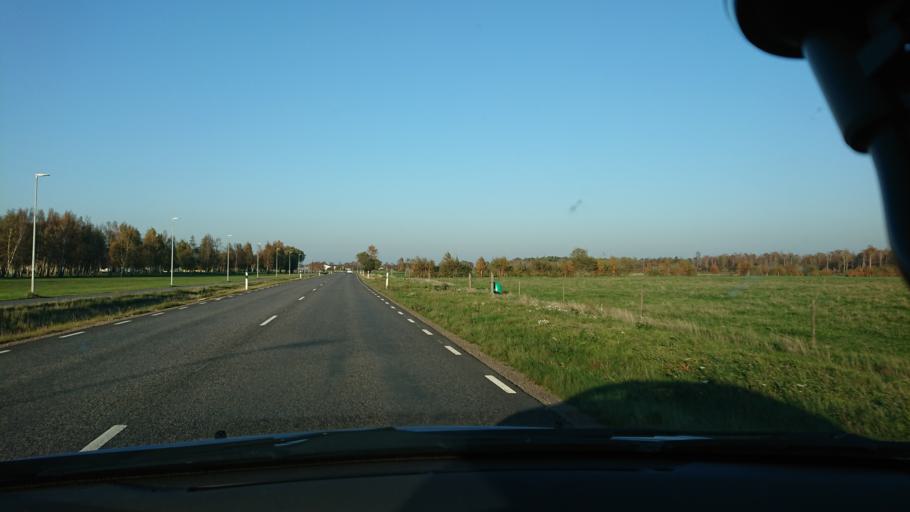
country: SE
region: Halland
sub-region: Laholms Kommun
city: Mellbystrand
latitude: 56.4476
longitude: 12.9314
